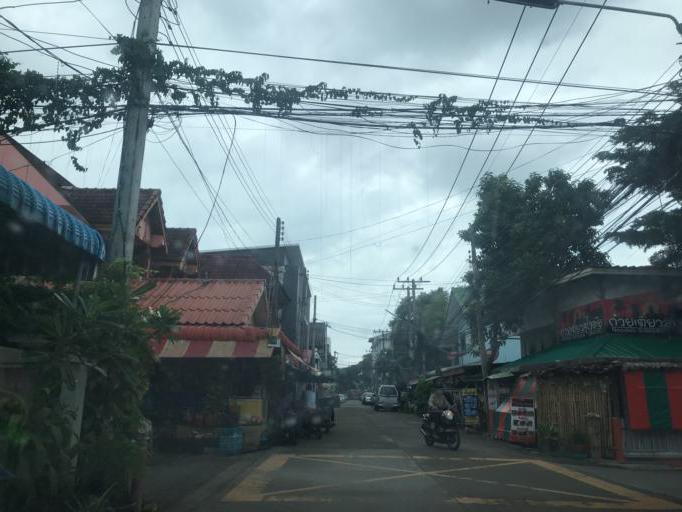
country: TH
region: Chiang Mai
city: Chiang Mai
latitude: 18.8046
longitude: 98.9745
